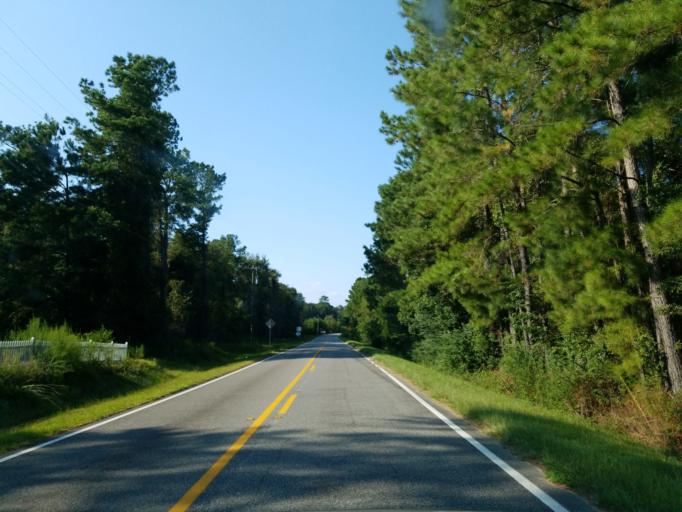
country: US
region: Georgia
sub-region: Lowndes County
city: Hahira
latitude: 31.0059
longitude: -83.3876
